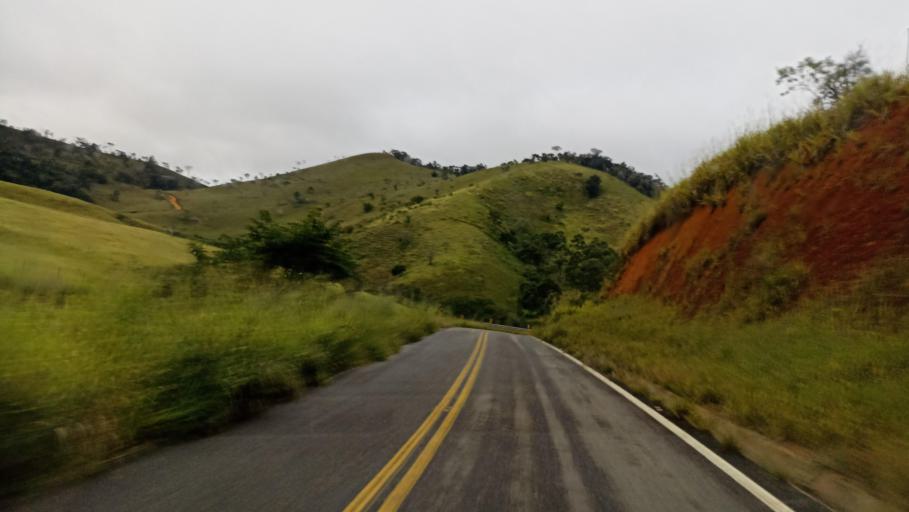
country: BR
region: Bahia
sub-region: Itanhem
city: Itanhem
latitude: -16.6907
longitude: -40.5111
